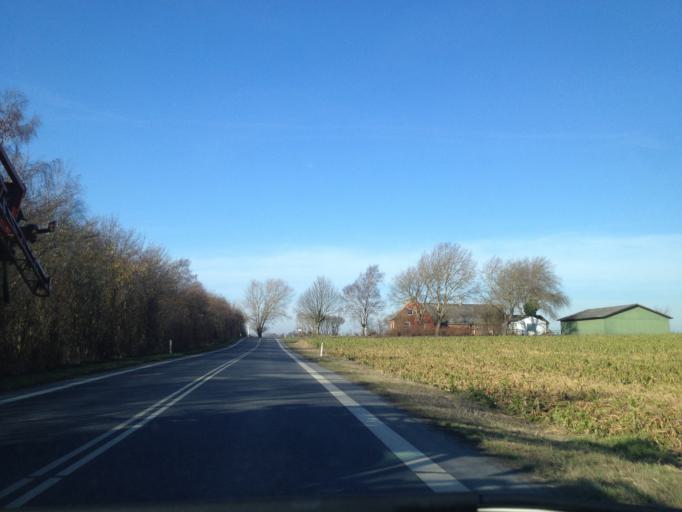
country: DK
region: South Denmark
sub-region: Kerteminde Kommune
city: Kerteminde
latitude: 55.4747
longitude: 10.6670
